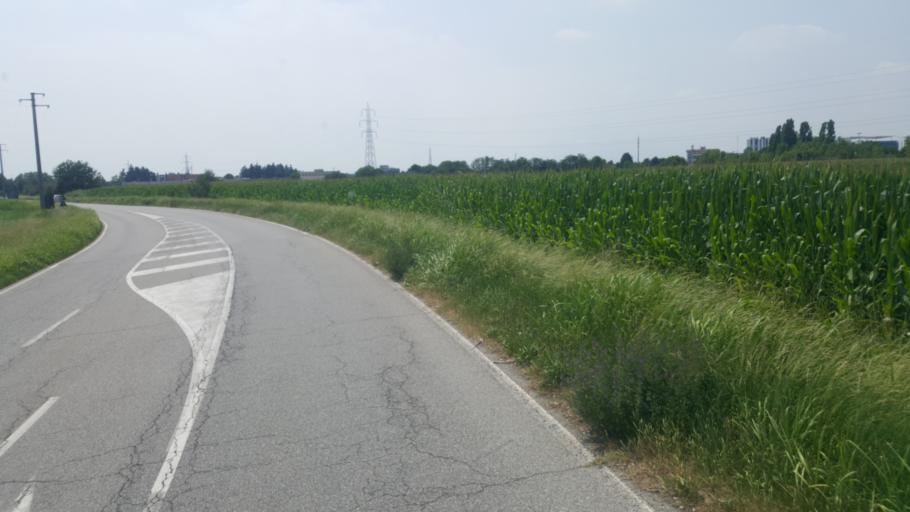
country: IT
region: Lombardy
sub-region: Provincia di Monza e Brianza
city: Burago di Molgora
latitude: 45.5956
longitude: 9.3689
